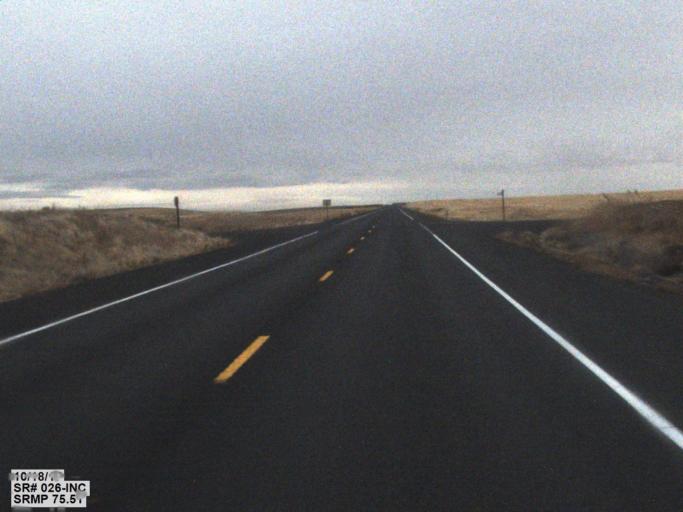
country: US
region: Washington
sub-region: Adams County
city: Ritzville
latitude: 46.7953
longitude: -118.4437
